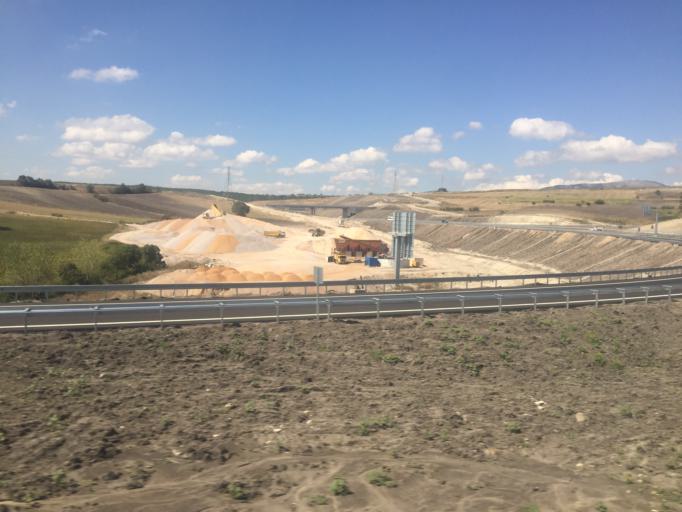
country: TR
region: Balikesir
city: Gobel
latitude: 39.9680
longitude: 28.1629
